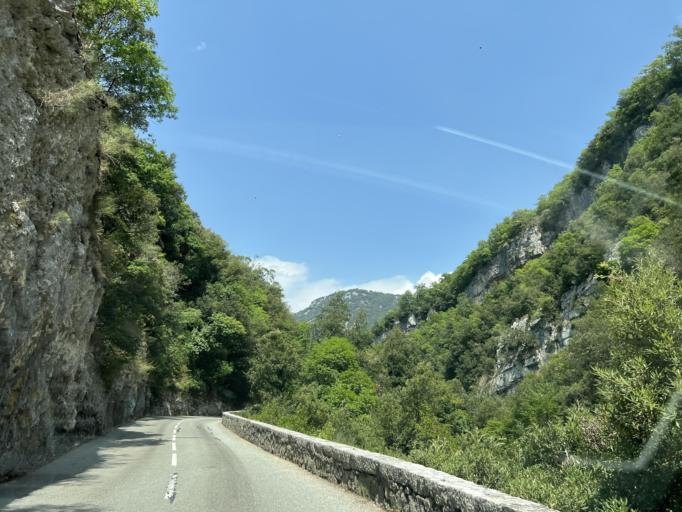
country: FR
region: Provence-Alpes-Cote d'Azur
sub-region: Departement des Alpes-Maritimes
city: Tourrettes-sur-Loup
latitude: 43.7433
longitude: 6.9992
